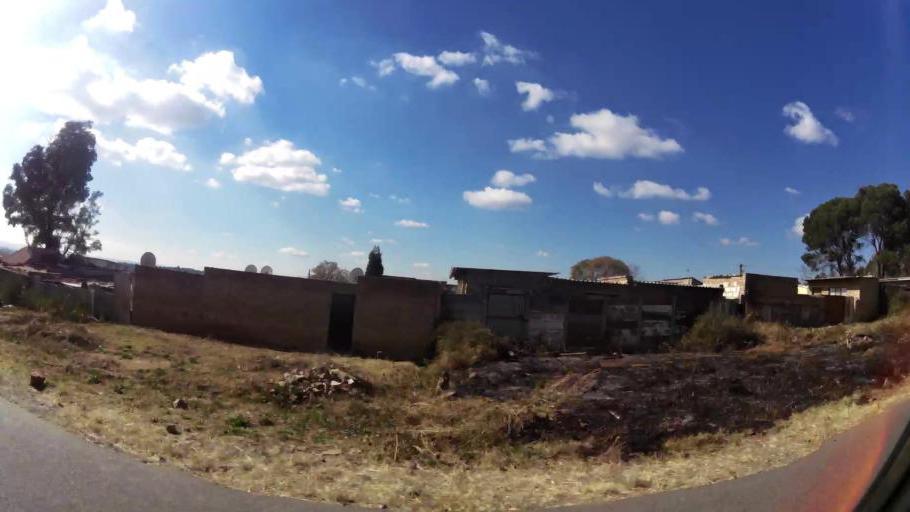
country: ZA
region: Gauteng
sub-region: West Rand District Municipality
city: Muldersdriseloop
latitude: -26.0518
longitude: 27.9054
